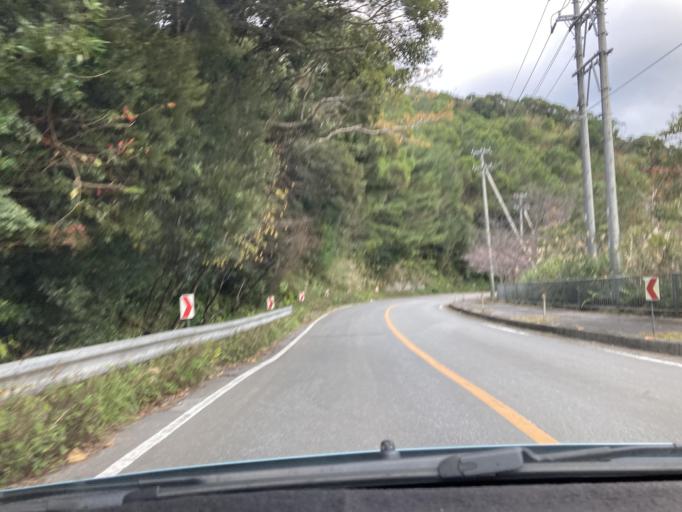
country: JP
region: Okinawa
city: Nago
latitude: 26.8310
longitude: 128.2737
